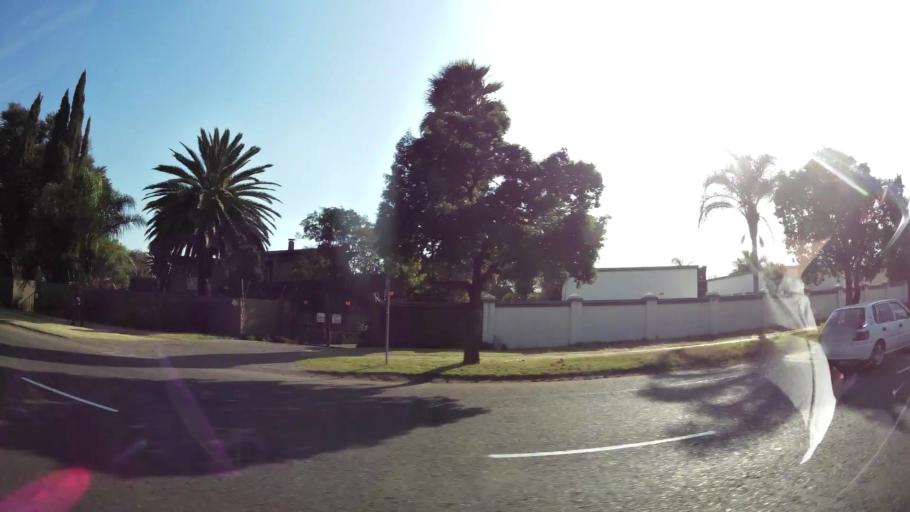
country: ZA
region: Gauteng
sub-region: West Rand District Municipality
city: Randfontein
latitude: -26.1684
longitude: 27.7119
